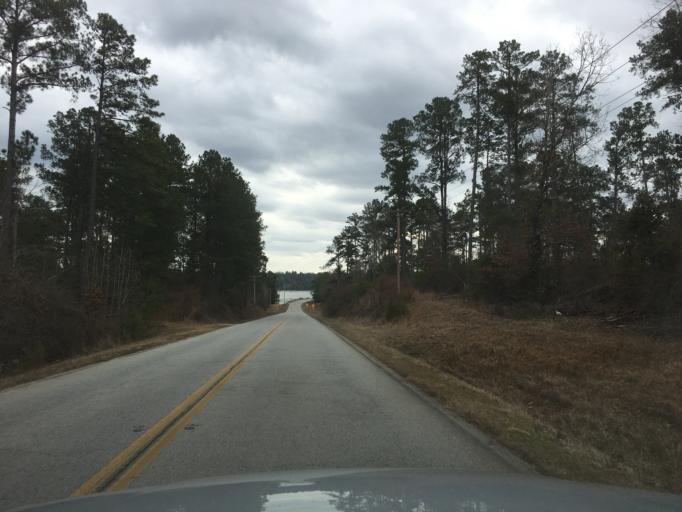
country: US
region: Georgia
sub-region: Lincoln County
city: Lincolnton
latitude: 33.8325
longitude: -82.4081
